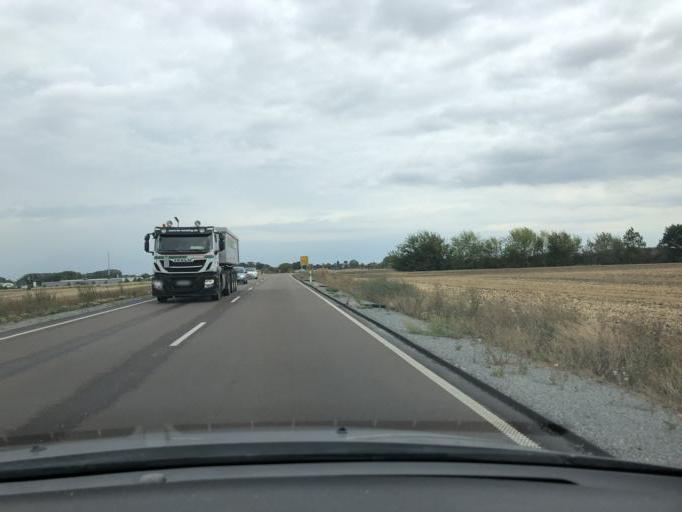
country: DE
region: Saxony-Anhalt
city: Brumby
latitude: 51.8956
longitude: 11.6964
